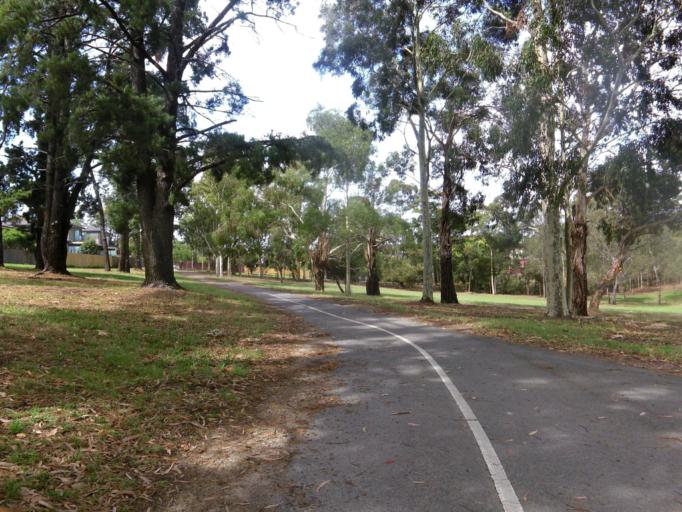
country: AU
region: Victoria
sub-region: Manningham
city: Doncaster
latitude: -37.7776
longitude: 145.1331
